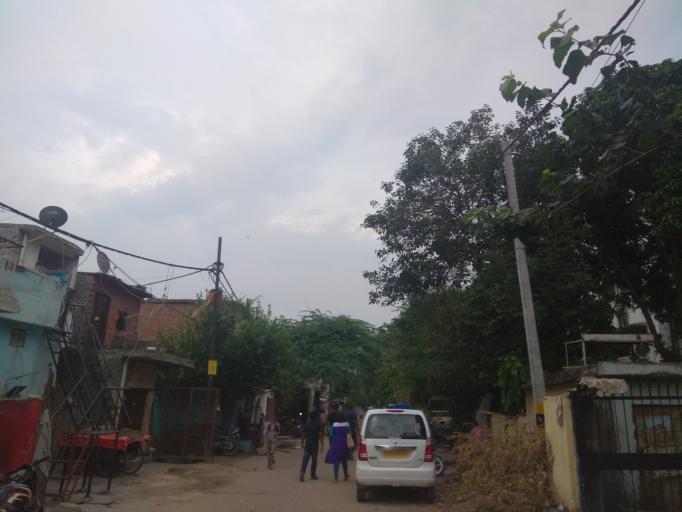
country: IN
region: NCT
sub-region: New Delhi
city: New Delhi
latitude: 28.5752
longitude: 77.2511
